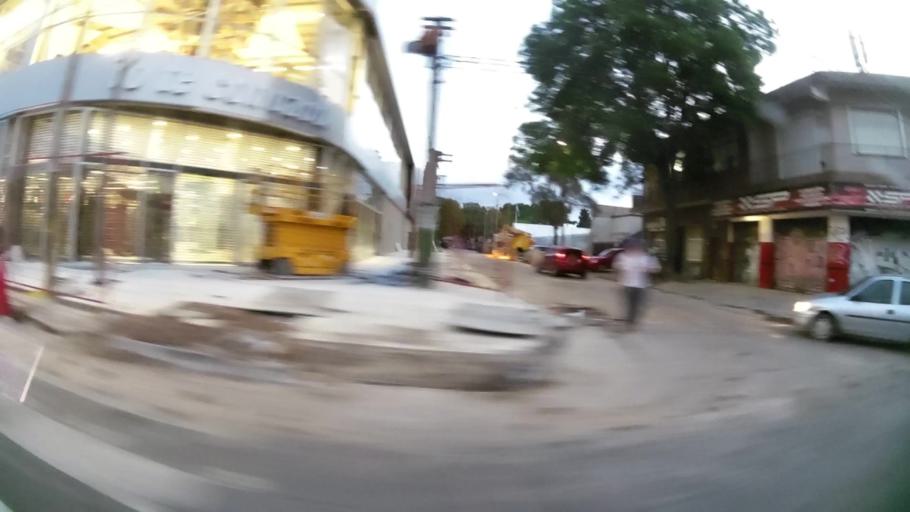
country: AR
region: Buenos Aires
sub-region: Partido de Merlo
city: Merlo
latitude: -34.6665
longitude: -58.7038
